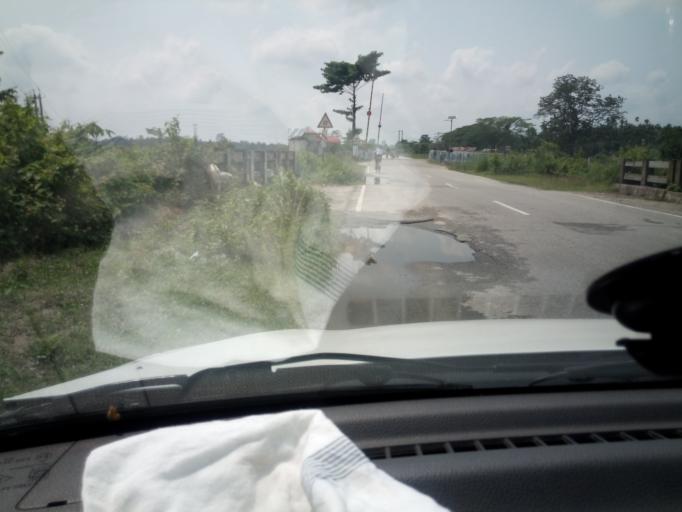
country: IN
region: Assam
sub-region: Udalguri
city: Udalguri
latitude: 26.7349
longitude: 92.1674
